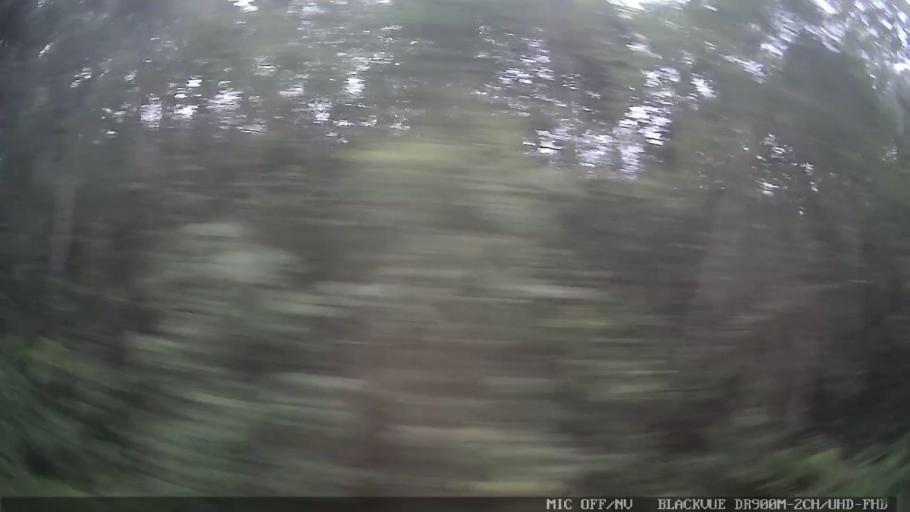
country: BR
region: Sao Paulo
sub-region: Rio Grande Da Serra
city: Rio Grande da Serra
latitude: -23.6881
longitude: -46.2612
